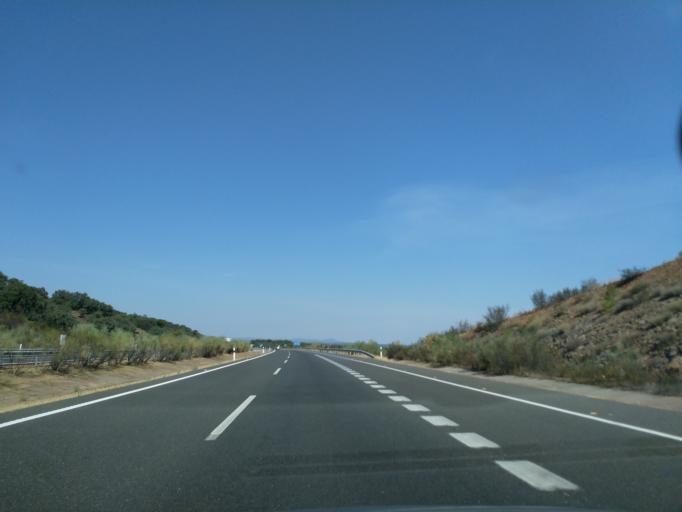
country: ES
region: Extremadura
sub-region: Provincia de Caceres
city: Alcuescar
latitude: 39.1698
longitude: -6.2701
